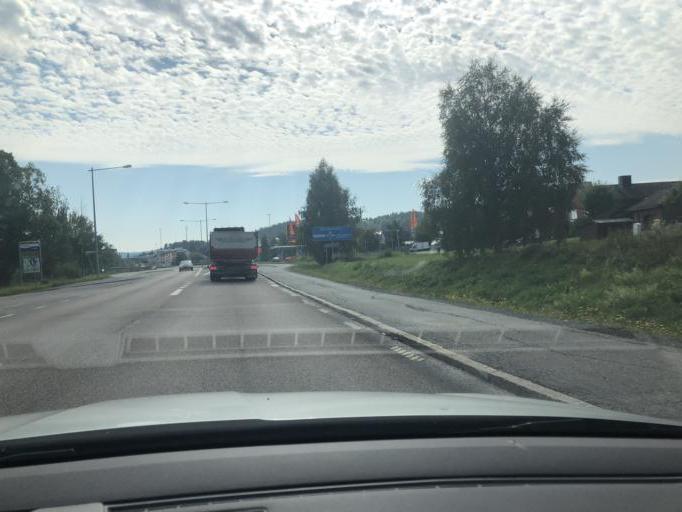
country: SE
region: Vaesternorrland
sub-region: Kramfors Kommun
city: Kramfors
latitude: 62.9361
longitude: 17.7704
